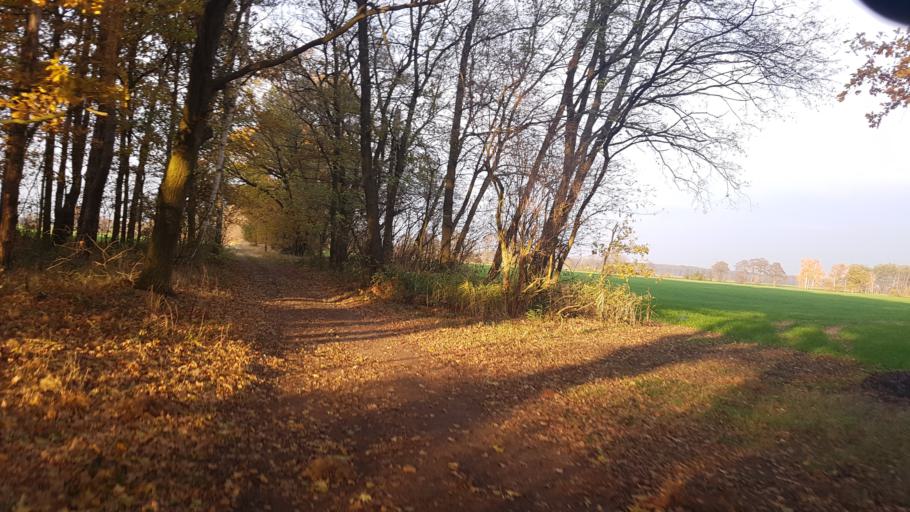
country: DE
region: Brandenburg
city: Schonewalde
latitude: 51.6448
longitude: 13.5999
